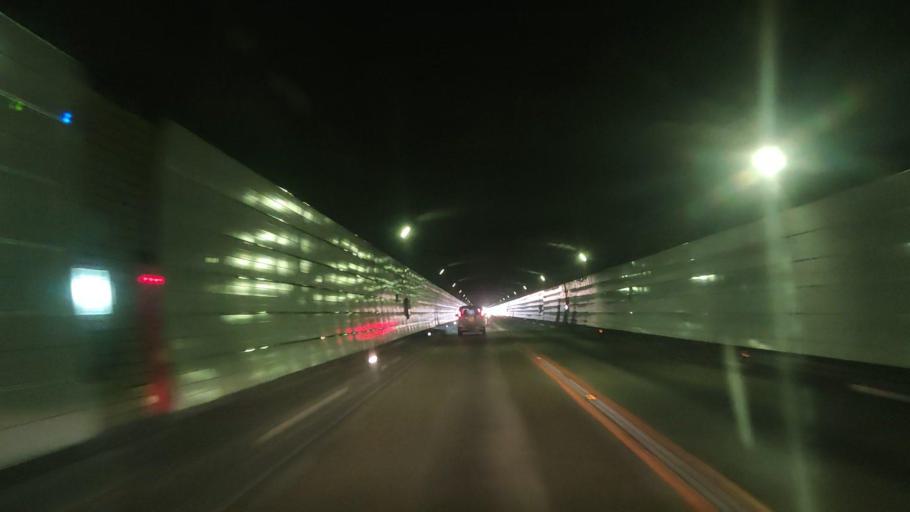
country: JP
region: Kumamoto
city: Hitoyoshi
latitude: 32.0951
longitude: 130.8029
